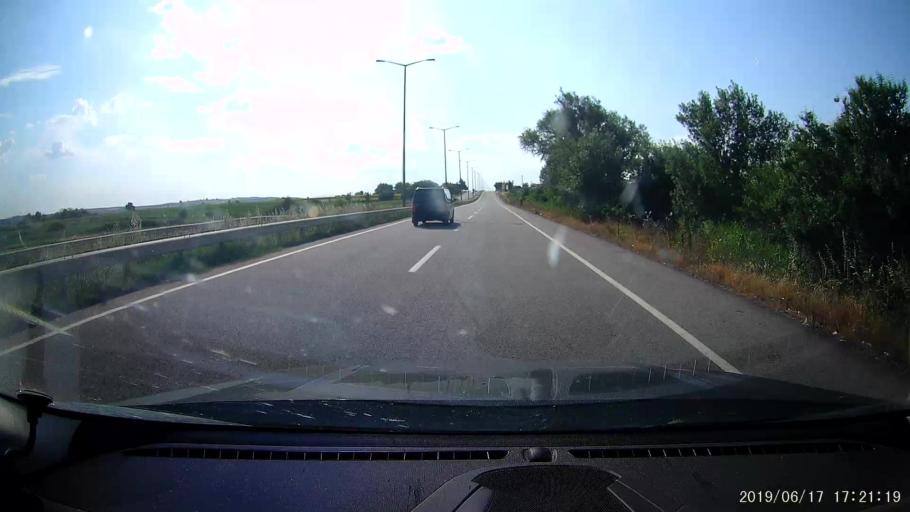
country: GR
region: East Macedonia and Thrace
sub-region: Nomos Evrou
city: Rizia
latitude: 41.7054
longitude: 26.3967
